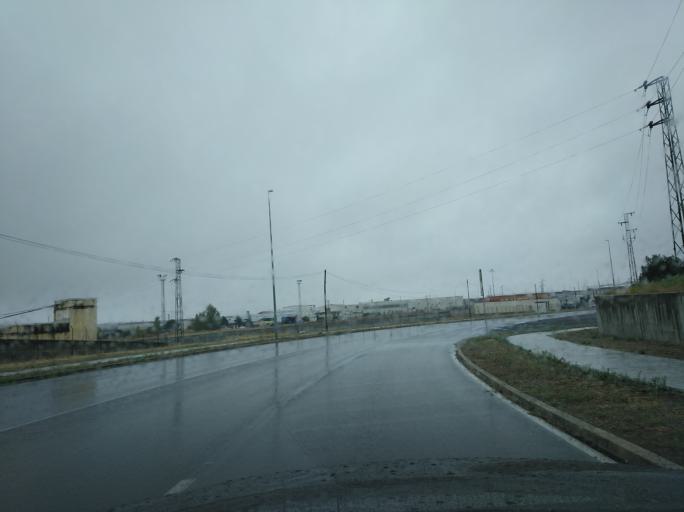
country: ES
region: Extremadura
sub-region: Provincia de Badajoz
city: Badajoz
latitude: 38.8947
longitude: -6.9854
